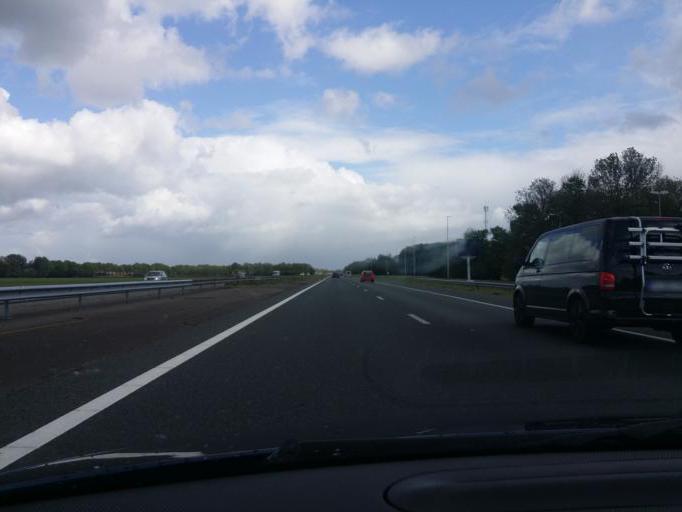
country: NL
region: Groningen
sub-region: Gemeente Hoogezand-Sappemeer
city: Hoogezand
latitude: 53.1949
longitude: 6.7006
